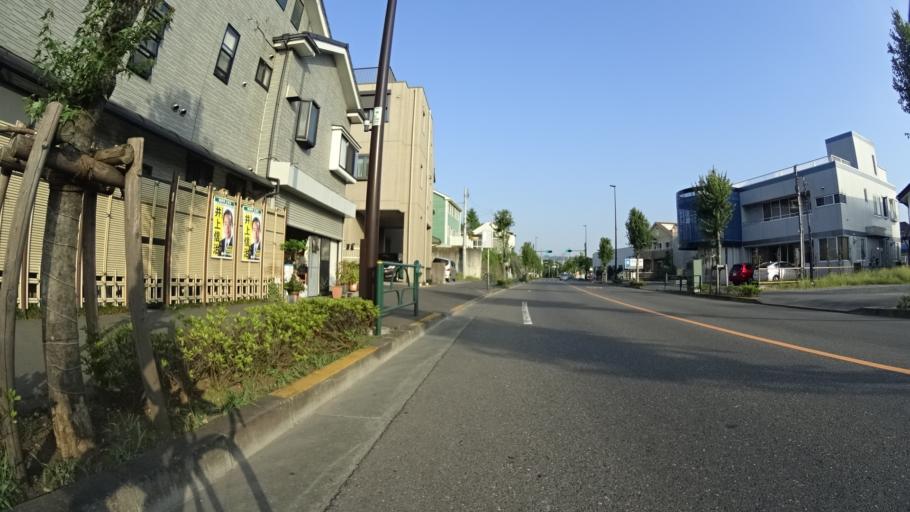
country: JP
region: Tokyo
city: Ome
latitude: 35.7746
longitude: 139.2813
